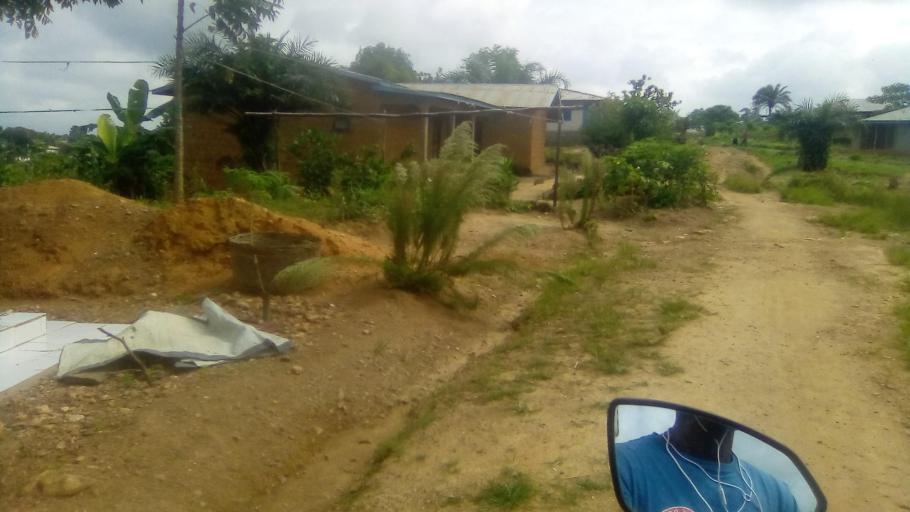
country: SL
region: Eastern Province
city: Kailahun
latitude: 8.2813
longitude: -10.5616
